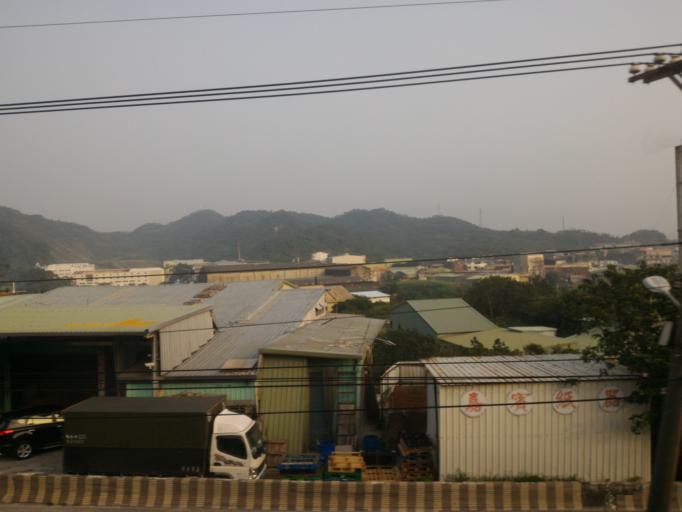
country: TW
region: Taiwan
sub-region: Taoyuan
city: Taoyuan
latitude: 24.9673
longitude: 121.3391
